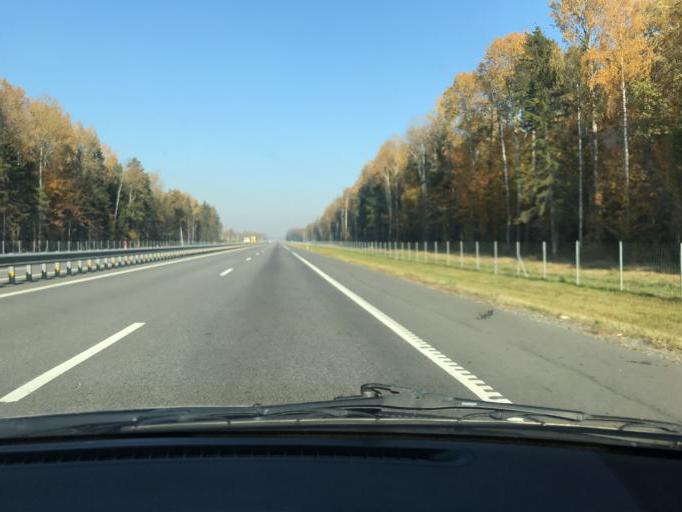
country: BY
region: Minsk
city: Slutsk
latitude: 53.2414
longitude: 27.5505
